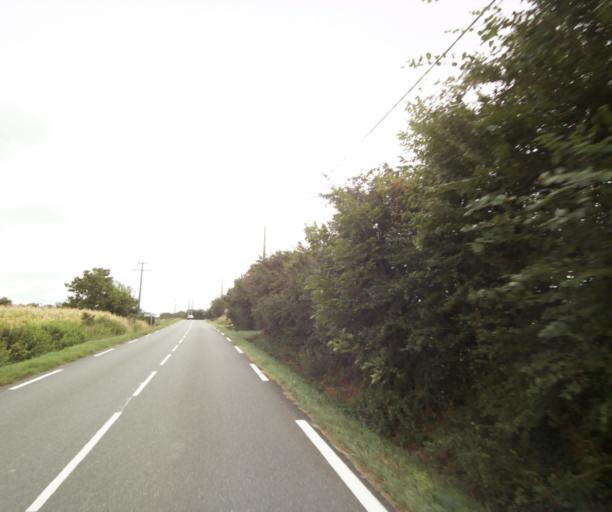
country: FR
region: Midi-Pyrenees
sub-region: Departement de la Haute-Garonne
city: Flourens
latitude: 43.5985
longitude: 1.5334
